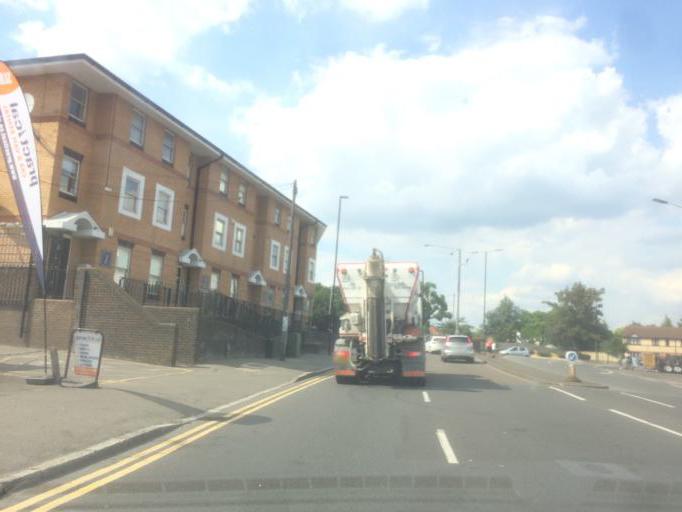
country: GB
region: England
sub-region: Buckinghamshire
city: Farnham Royal
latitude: 51.5286
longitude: -0.6169
